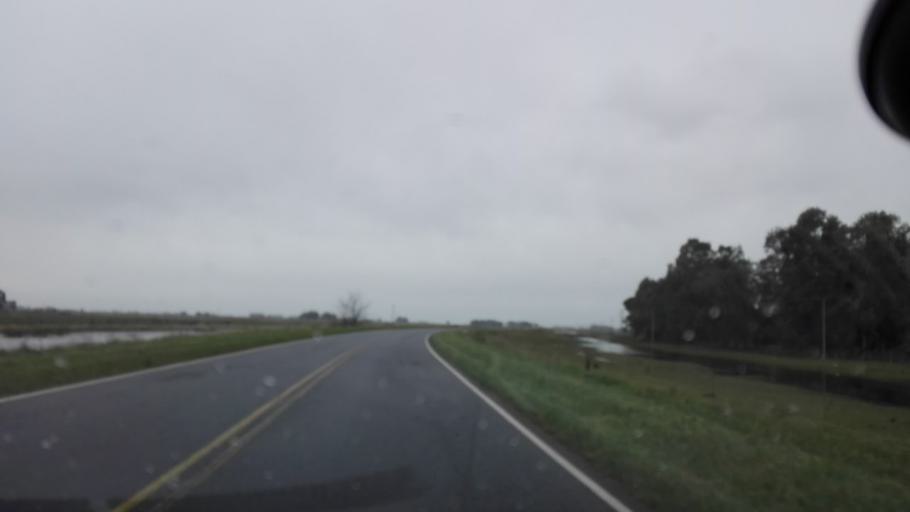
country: AR
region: Buenos Aires
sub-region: Partido de Rauch
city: Rauch
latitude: -36.8873
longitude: -58.9912
